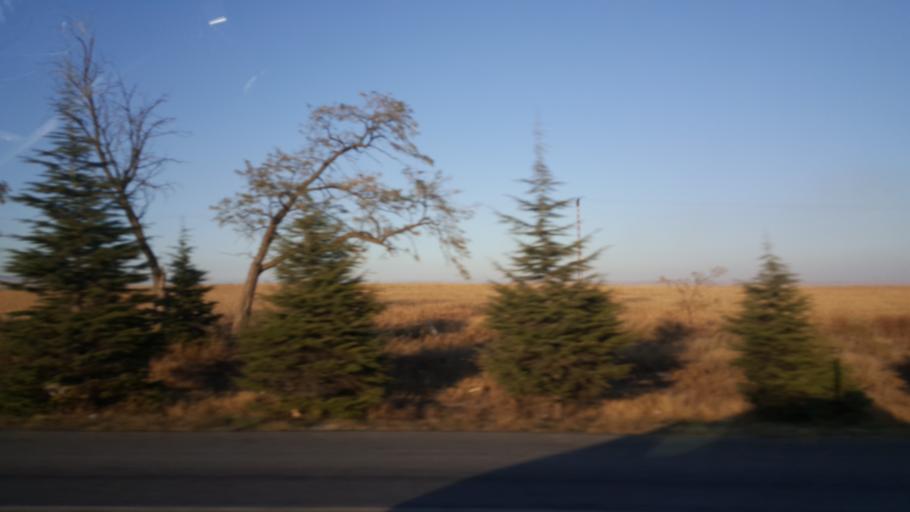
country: TR
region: Eskisehir
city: Mahmudiye
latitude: 39.5840
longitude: 30.9031
